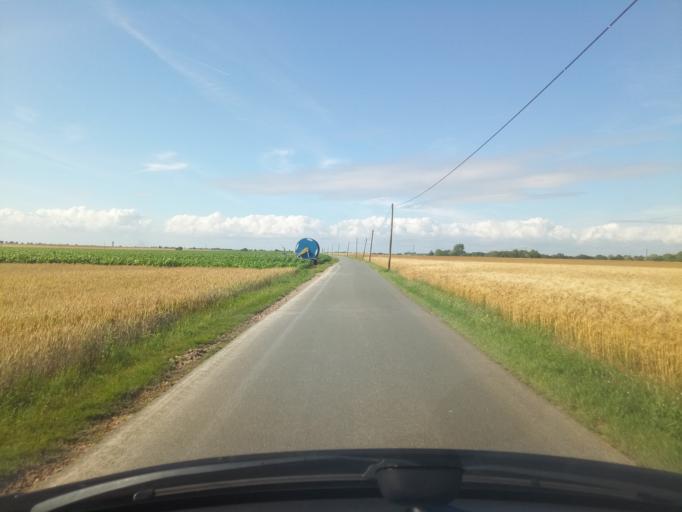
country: FR
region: Poitou-Charentes
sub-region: Departement de la Charente-Maritime
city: Andilly
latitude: 46.2362
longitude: -0.9993
